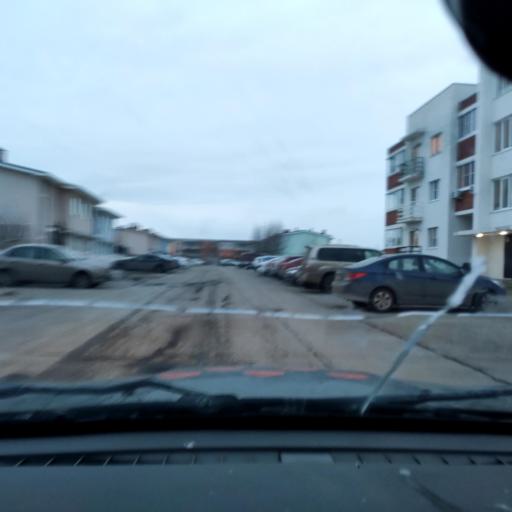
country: RU
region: Samara
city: Tol'yatti
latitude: 53.6195
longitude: 49.3173
